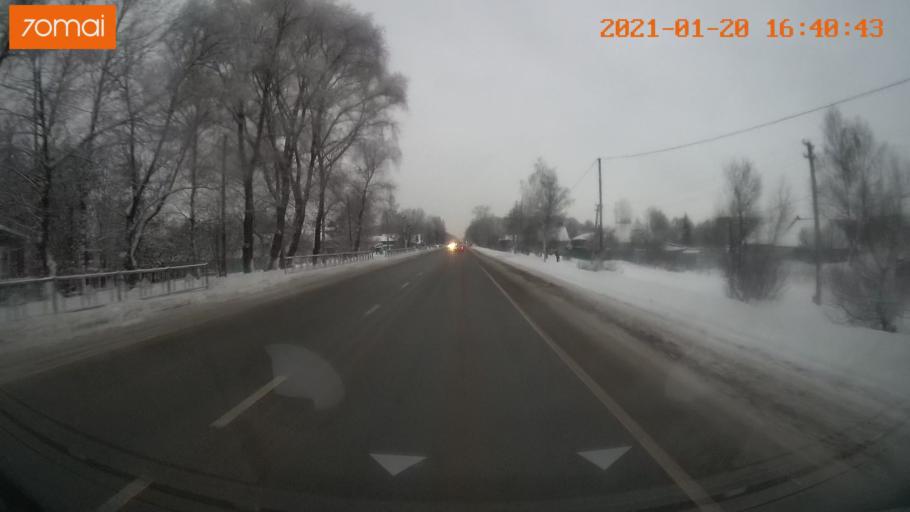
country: RU
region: Vladimir
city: Orgtrud
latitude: 56.2098
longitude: 40.6637
